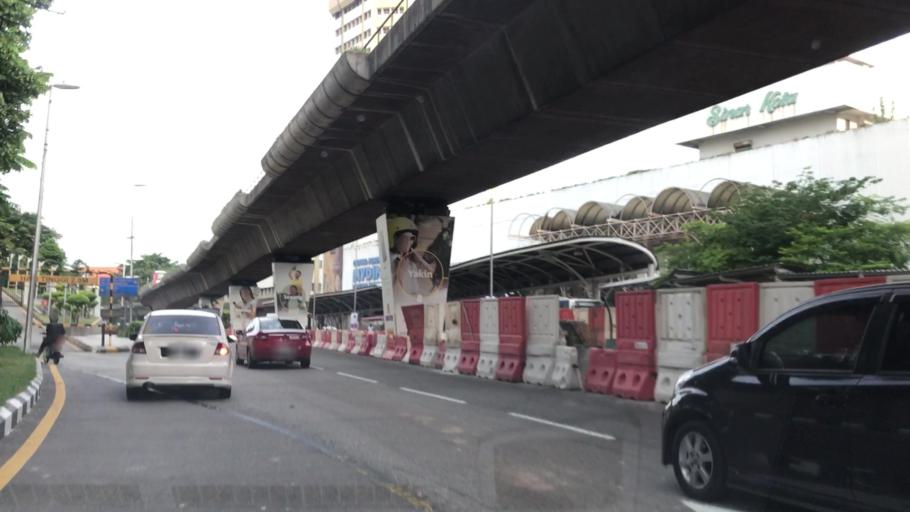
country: MY
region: Kuala Lumpur
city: Kuala Lumpur
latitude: 3.1475
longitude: 101.6983
